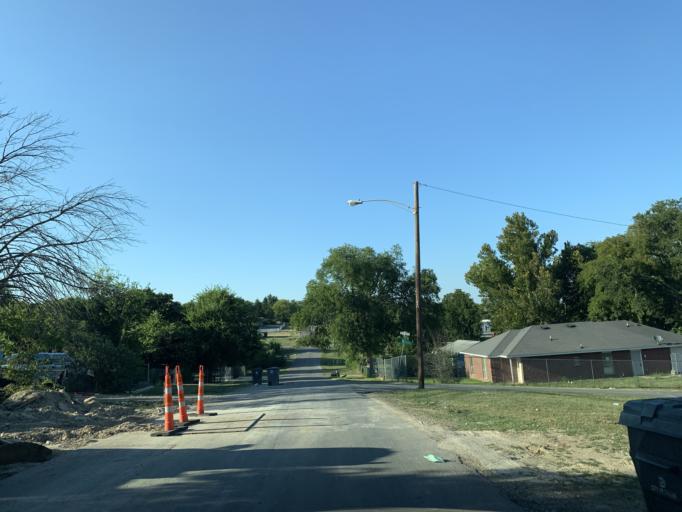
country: US
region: Texas
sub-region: Dallas County
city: Hutchins
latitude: 32.6683
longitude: -96.7782
